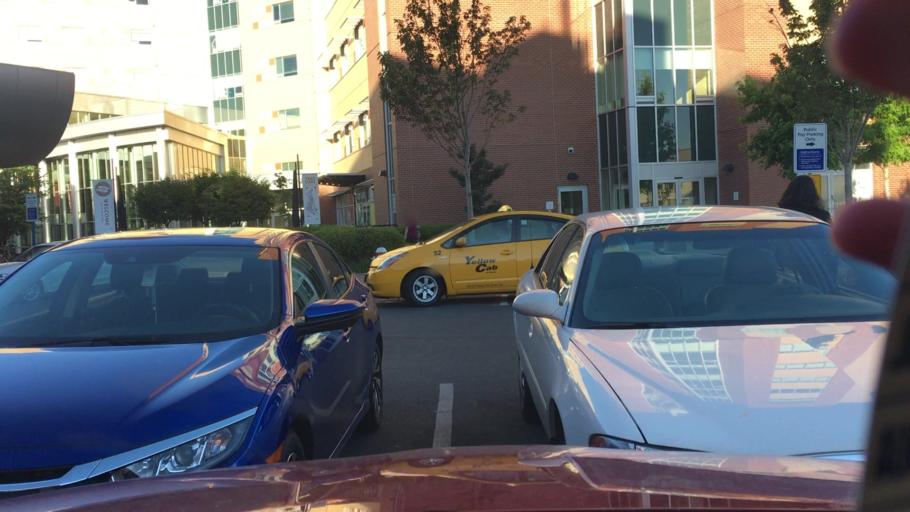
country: CA
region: British Columbia
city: Oak Bay
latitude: 48.4336
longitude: -123.3272
